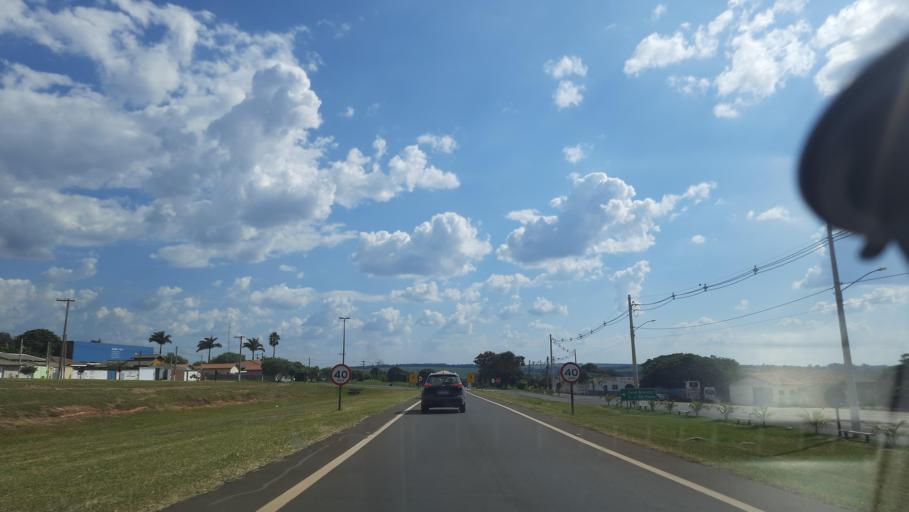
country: BR
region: Sao Paulo
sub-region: Casa Branca
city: Casa Branca
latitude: -21.7357
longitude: -46.9720
